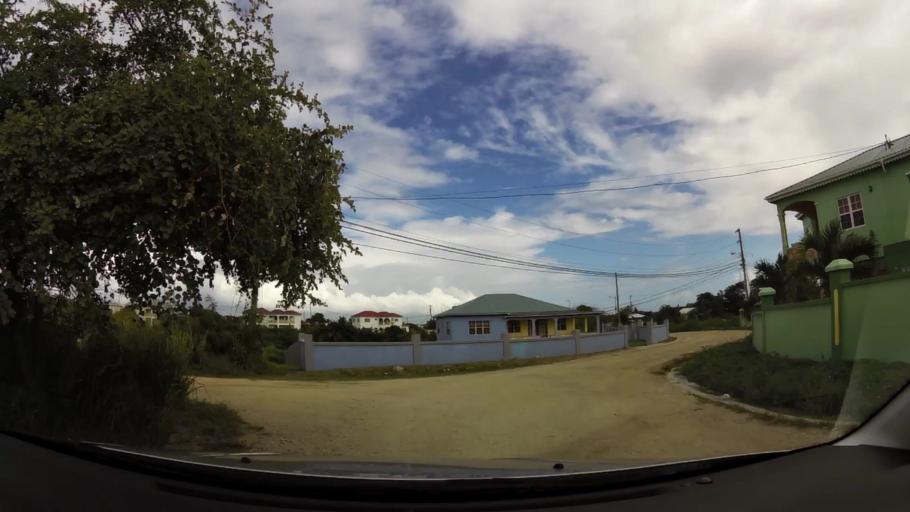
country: AG
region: Saint George
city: Piggotts
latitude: 17.1052
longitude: -61.8117
